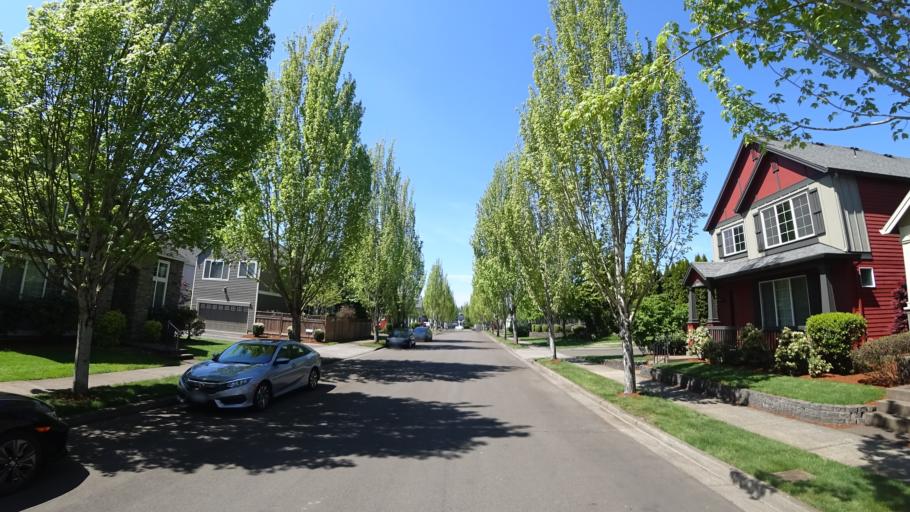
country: US
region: Oregon
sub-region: Washington County
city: Hillsboro
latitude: 45.5080
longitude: -122.9734
